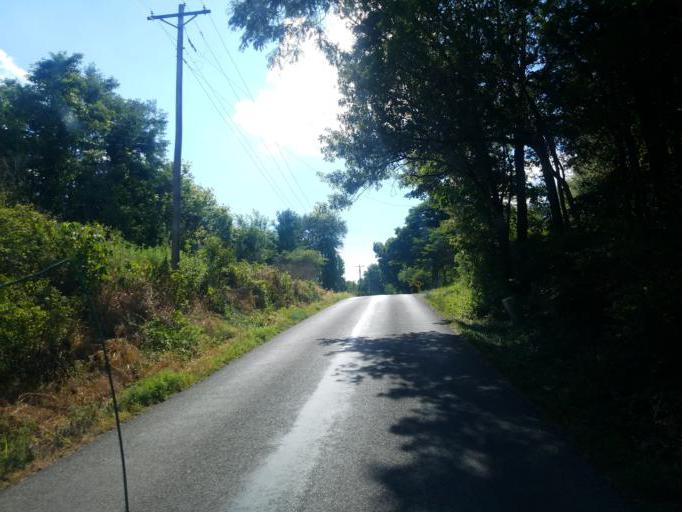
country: US
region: Illinois
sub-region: Jackson County
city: Murphysboro
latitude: 37.7163
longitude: -89.2985
